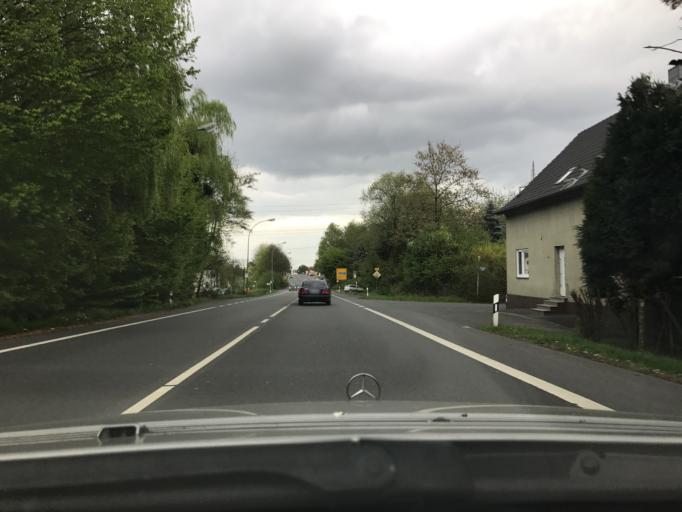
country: DE
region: North Rhine-Westphalia
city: Lunen
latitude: 51.5893
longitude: 7.4743
